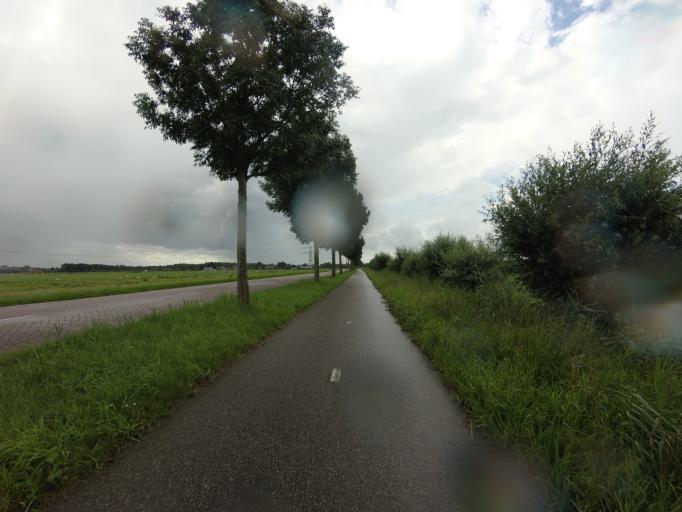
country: NL
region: Utrecht
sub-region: Gemeente Utrecht
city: Utrecht
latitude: 52.1451
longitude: 5.1198
